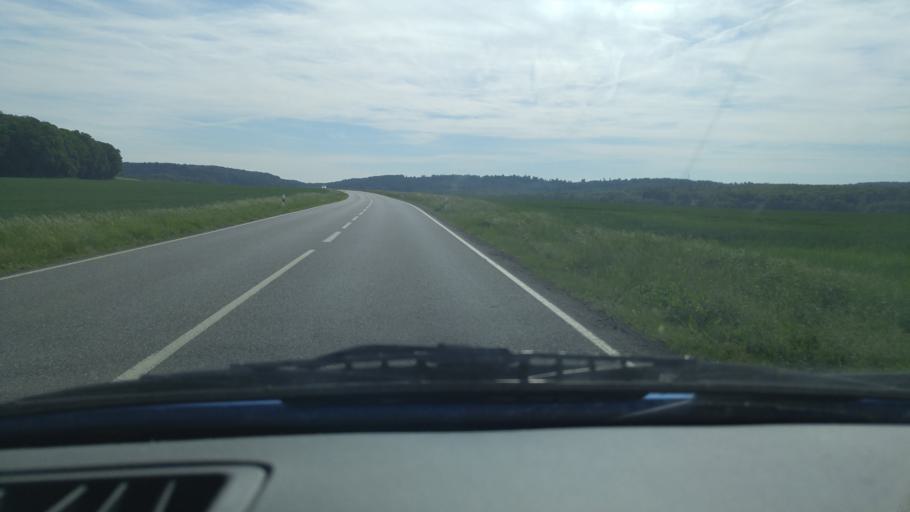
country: DE
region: Hesse
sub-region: Regierungsbezirk Darmstadt
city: Echzell
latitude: 50.4155
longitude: 8.9112
